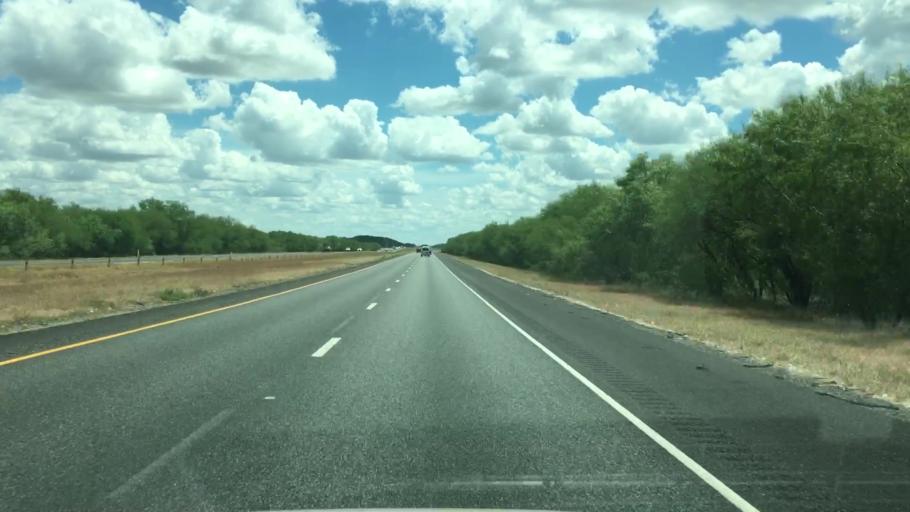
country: US
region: Texas
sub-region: Atascosa County
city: Pleasanton
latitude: 28.7444
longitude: -98.2931
